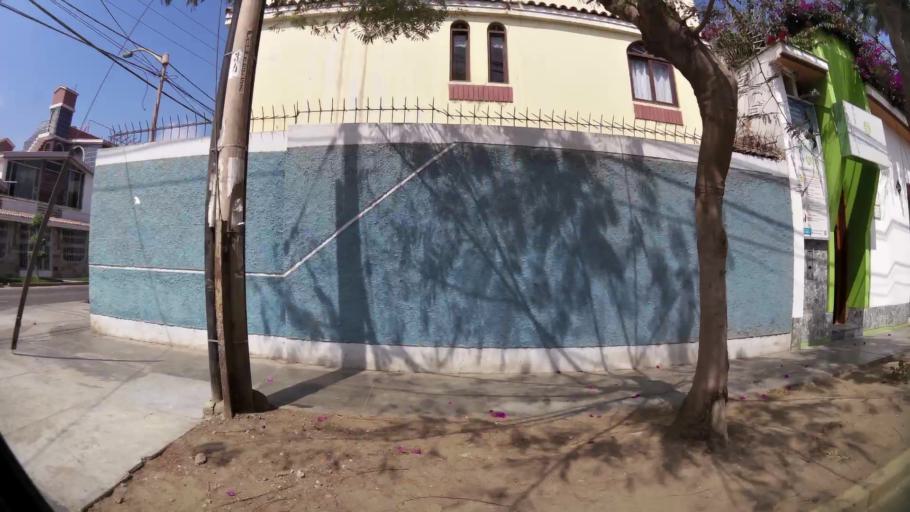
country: PE
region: La Libertad
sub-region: Provincia de Trujillo
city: Buenos Aires
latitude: -8.1267
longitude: -79.0380
